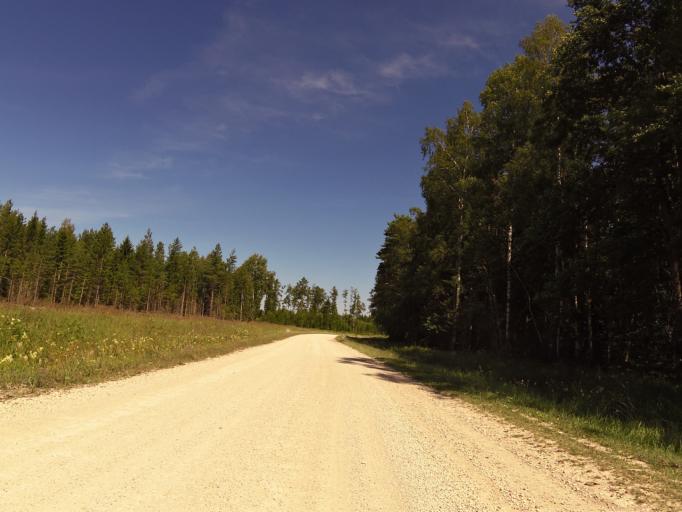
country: EE
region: Hiiumaa
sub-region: Kaerdla linn
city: Kardla
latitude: 58.9250
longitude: 22.3679
